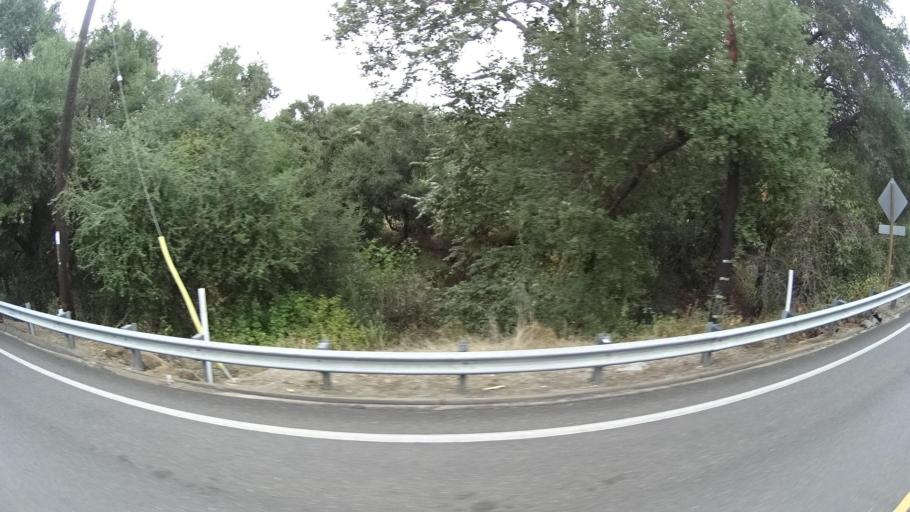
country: US
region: California
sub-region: San Diego County
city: Ramona
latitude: 33.0735
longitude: -116.9027
